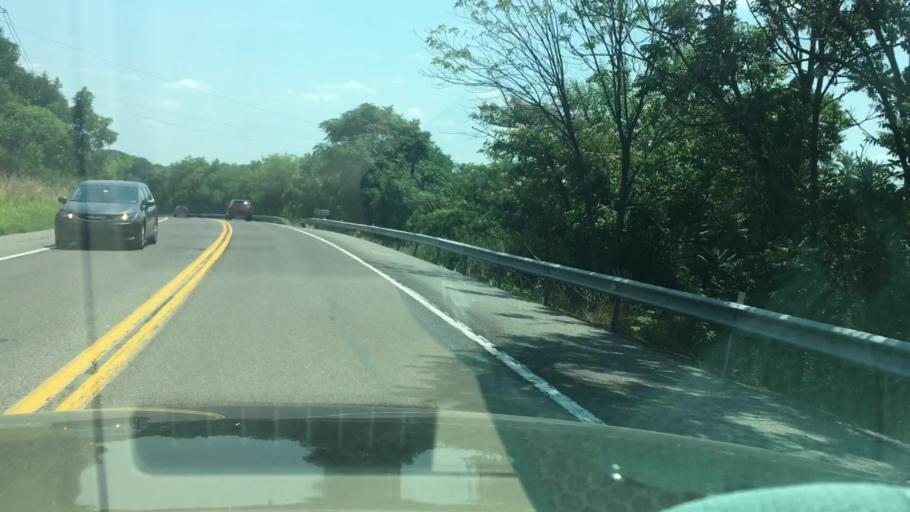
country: US
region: Pennsylvania
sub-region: Lehigh County
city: Trexlertown
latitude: 40.6033
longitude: -75.6391
